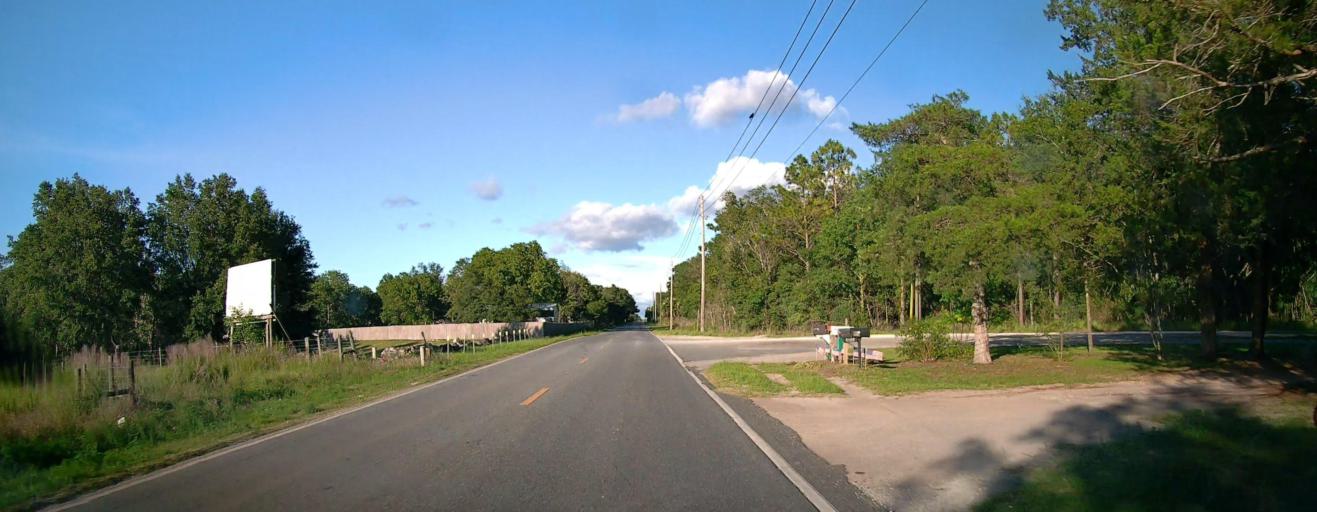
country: US
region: Florida
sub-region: Marion County
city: Silver Springs Shores
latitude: 29.0650
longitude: -82.0127
